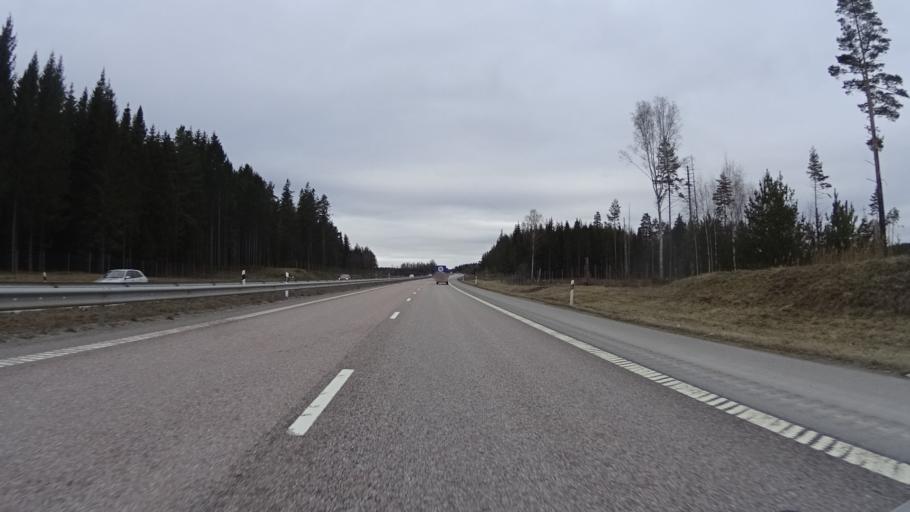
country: SE
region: Soedermanland
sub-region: Strangnas Kommun
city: Akers Styckebruk
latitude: 59.3081
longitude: 17.0694
